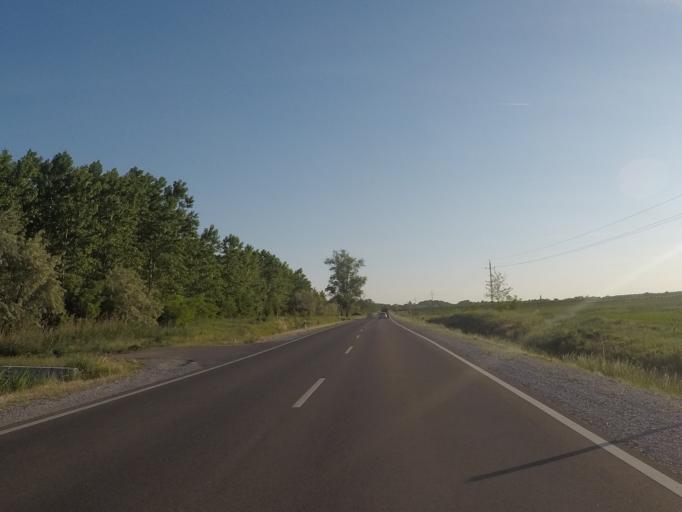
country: HU
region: Heves
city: Erdotelek
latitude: 47.6668
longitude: 20.3591
